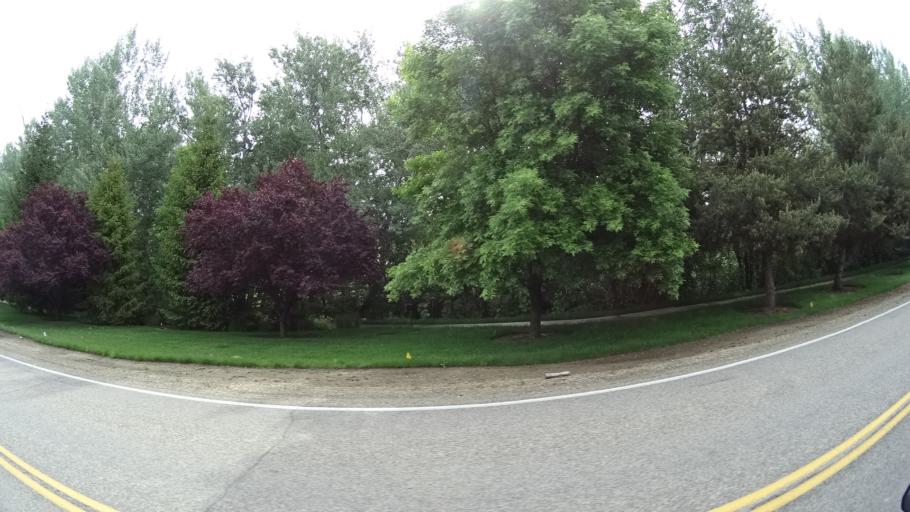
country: US
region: Idaho
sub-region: Ada County
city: Eagle
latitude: 43.7043
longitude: -116.3791
